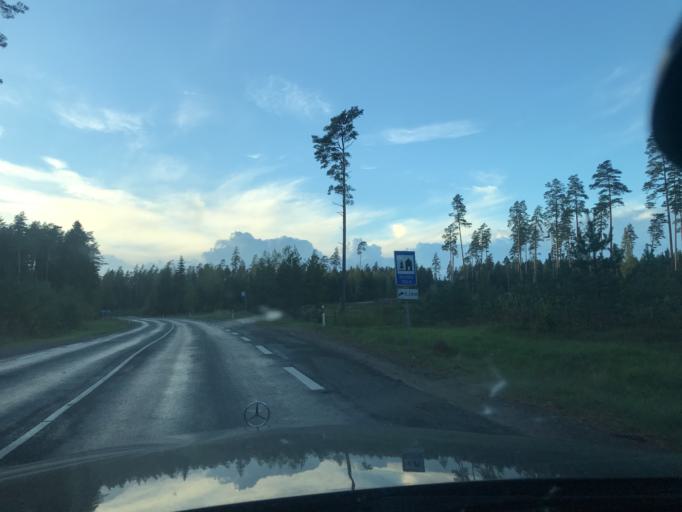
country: EE
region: Vorumaa
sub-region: Antsla vald
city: Vana-Antsla
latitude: 57.8787
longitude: 26.7678
